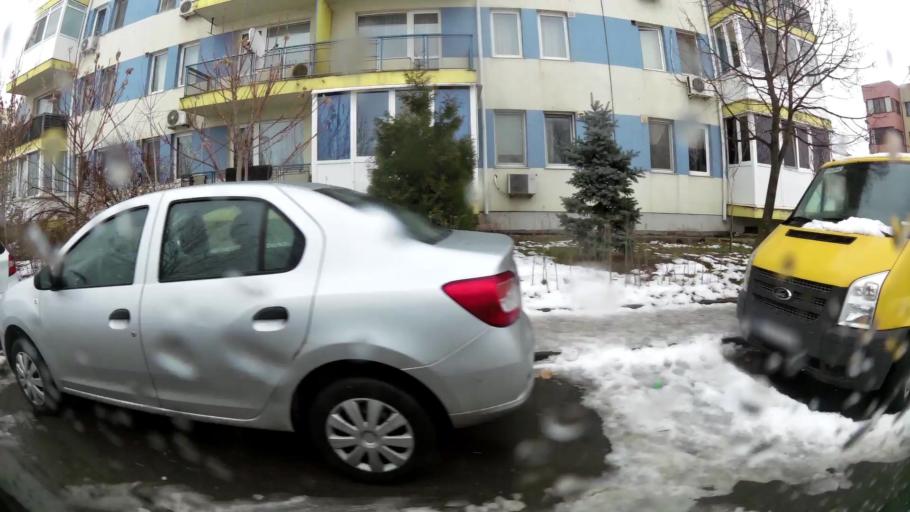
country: RO
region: Ilfov
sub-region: Comuna Chiajna
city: Rosu
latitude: 44.4187
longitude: 26.0073
